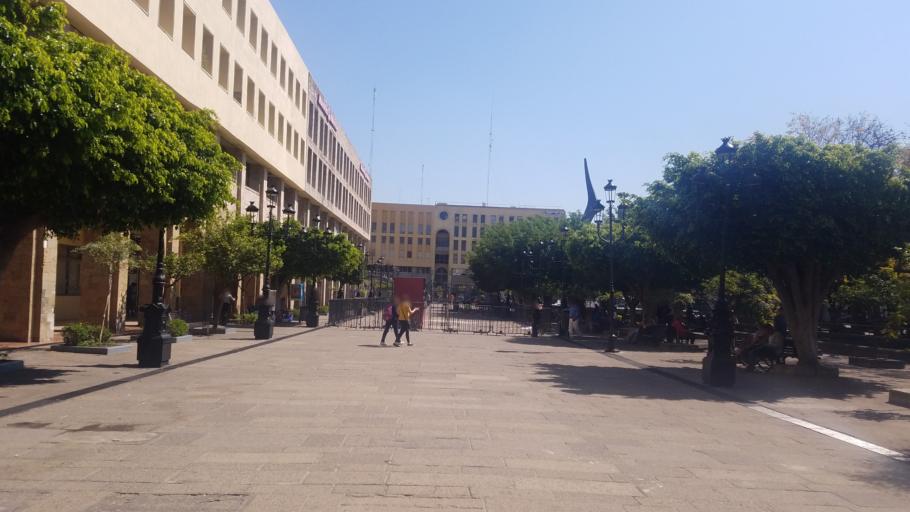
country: MX
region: Jalisco
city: Guadalajara
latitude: 20.6771
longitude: -103.3419
